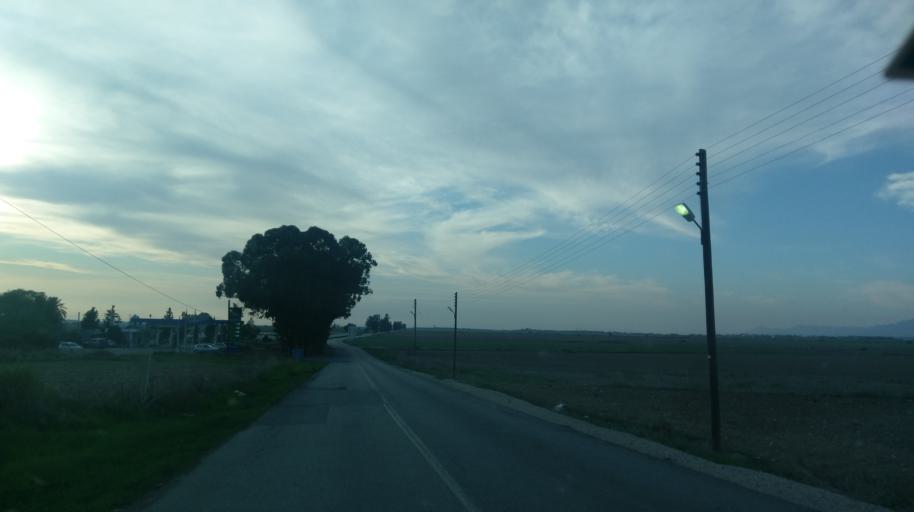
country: CY
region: Larnaka
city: Athienou
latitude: 35.1567
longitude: 33.5704
